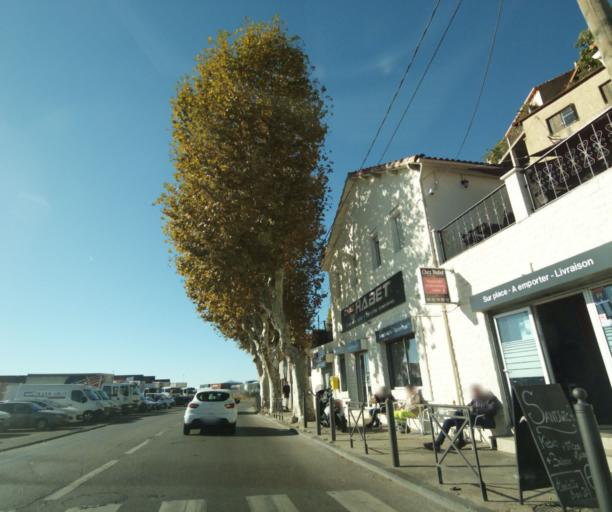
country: FR
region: Provence-Alpes-Cote d'Azur
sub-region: Departement des Bouches-du-Rhone
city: Marseille 16
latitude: 43.3541
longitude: 5.3324
